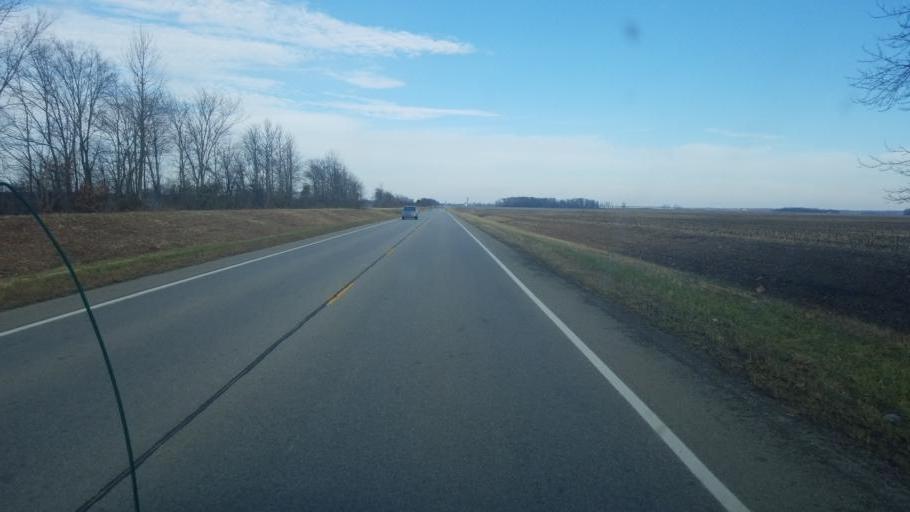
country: US
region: Illinois
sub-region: White County
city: Carmi
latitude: 38.1228
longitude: -88.1082
